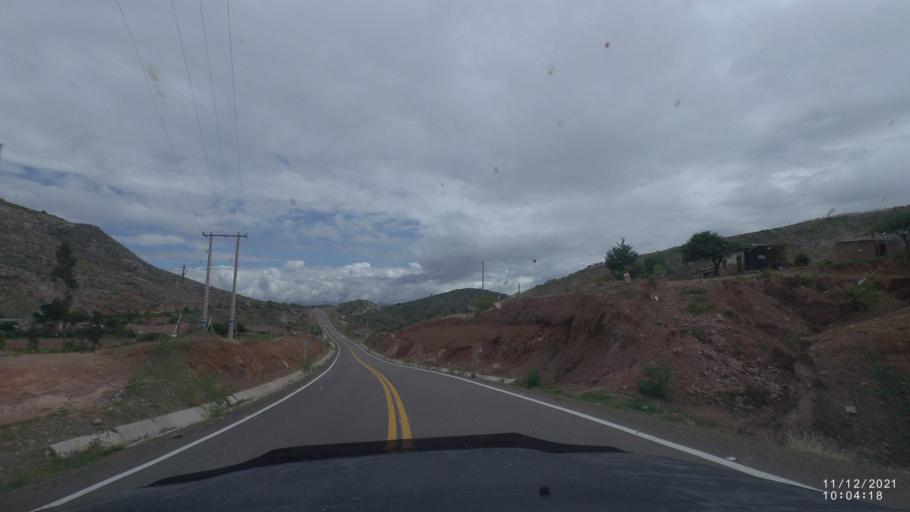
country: BO
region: Cochabamba
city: Cliza
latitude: -17.7119
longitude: -65.9423
